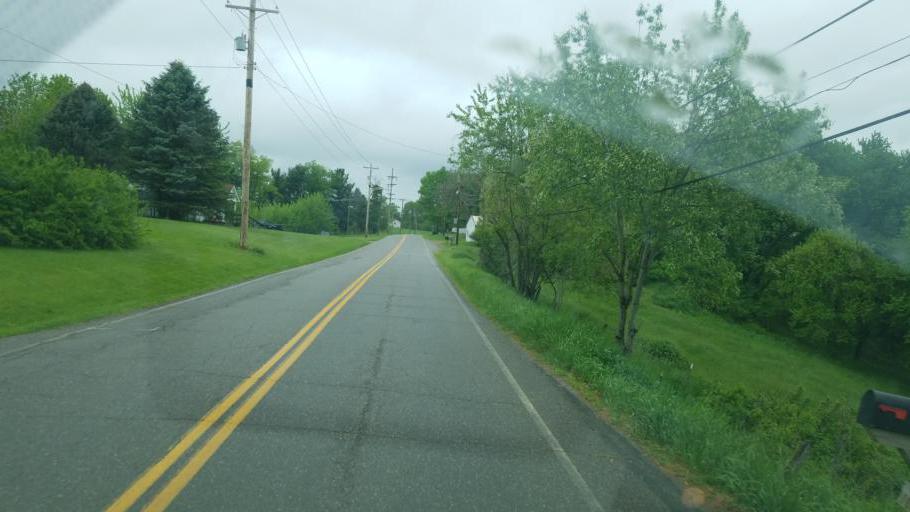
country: US
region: Ohio
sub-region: Jefferson County
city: Tiltonsville
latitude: 40.2587
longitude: -80.7588
